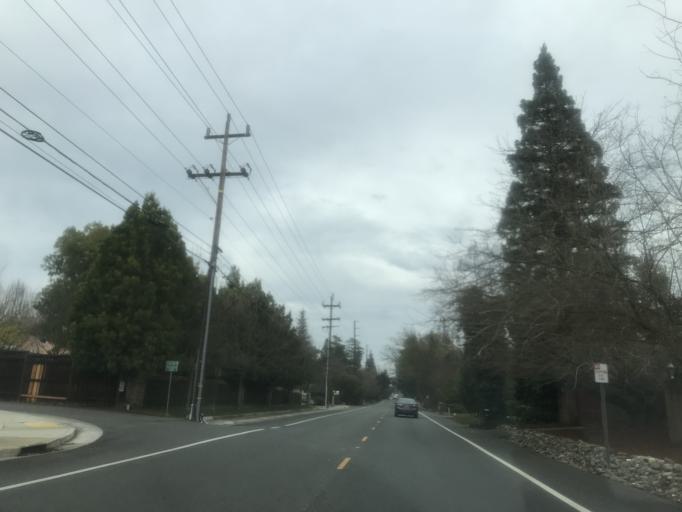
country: US
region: California
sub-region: Sacramento County
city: Arden-Arcade
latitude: 38.5815
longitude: -121.3996
